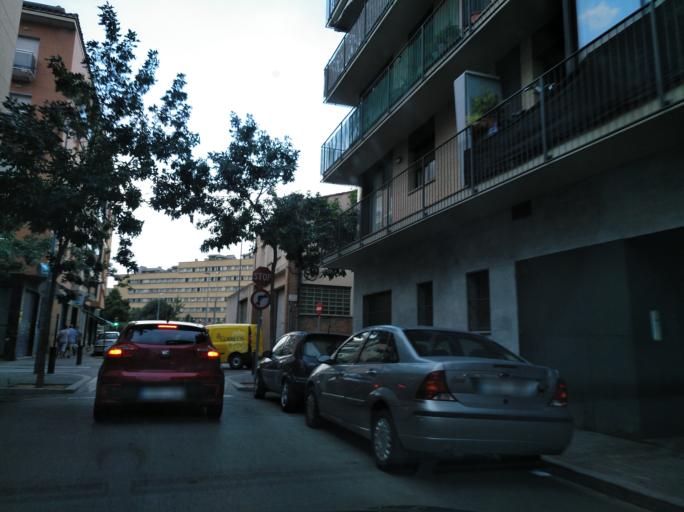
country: ES
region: Catalonia
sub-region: Provincia de Girona
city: Salt
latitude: 41.9764
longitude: 2.8069
